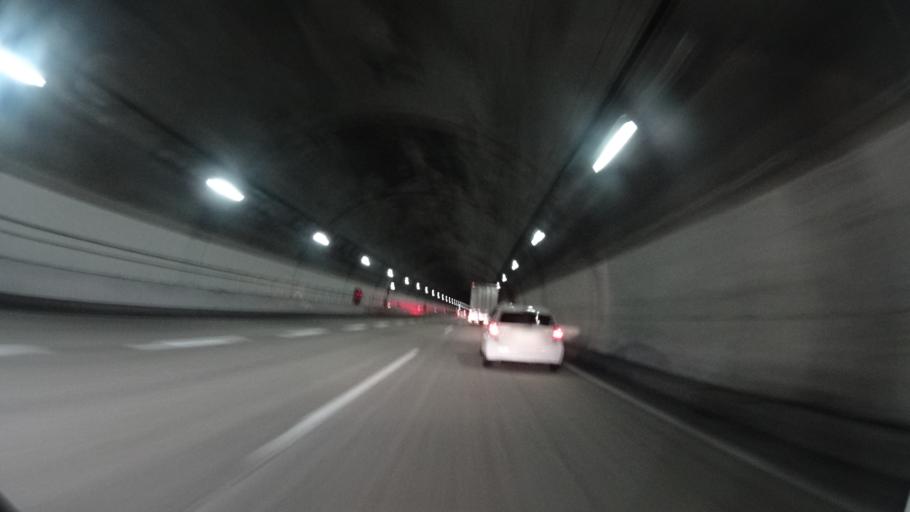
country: JP
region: Hyogo
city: Miki
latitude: 34.8105
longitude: 135.0236
